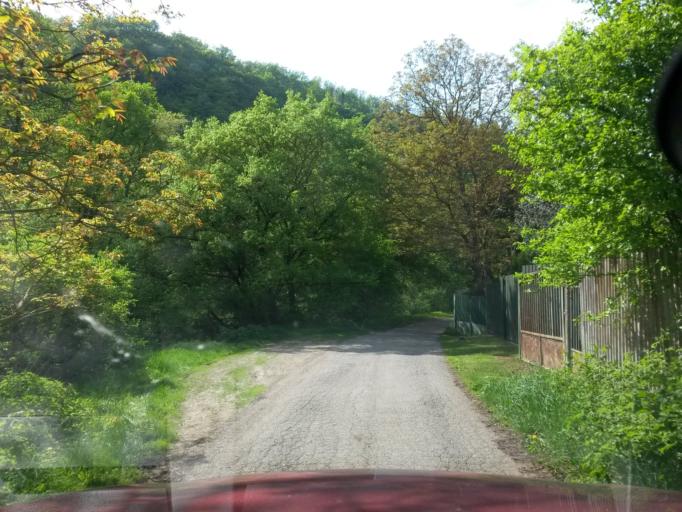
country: SK
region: Kosicky
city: Kosice
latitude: 48.7668
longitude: 21.2409
